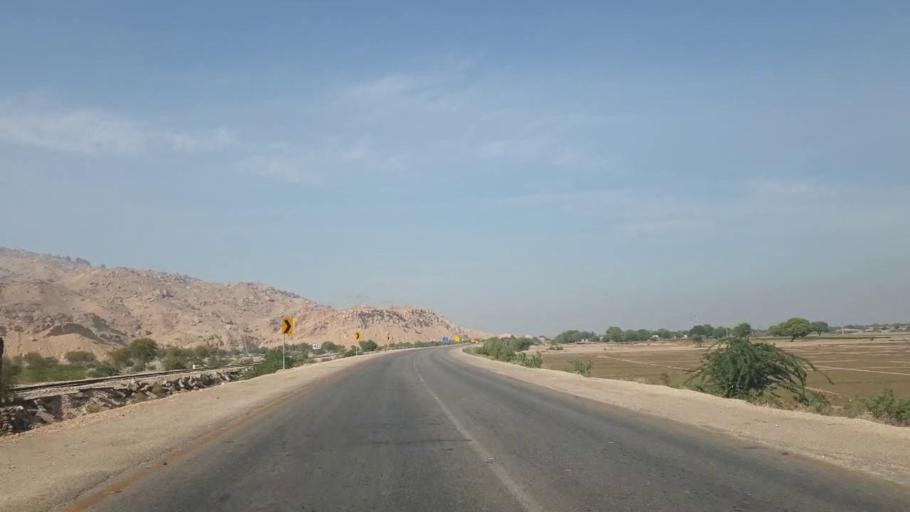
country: PK
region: Sindh
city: Sehwan
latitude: 26.2855
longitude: 67.8949
